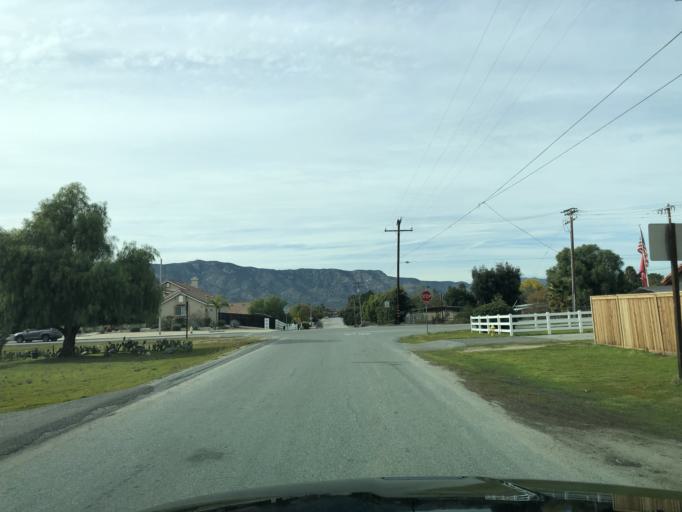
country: US
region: California
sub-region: Riverside County
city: Wildomar
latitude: 33.6160
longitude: -117.2749
